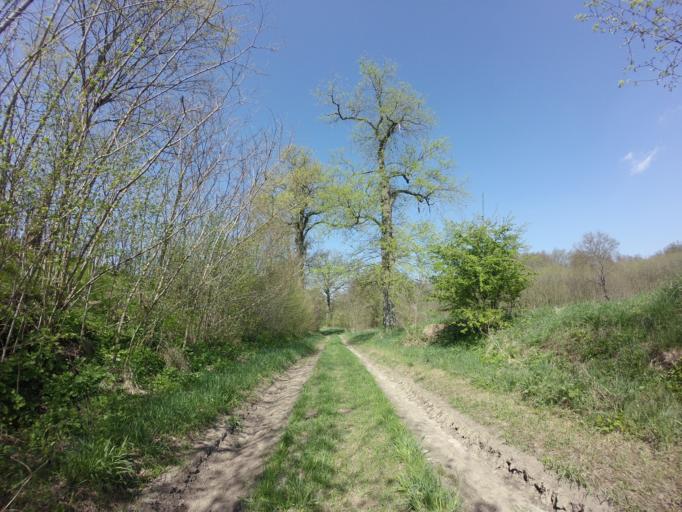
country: PL
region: West Pomeranian Voivodeship
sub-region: Powiat stargardzki
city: Suchan
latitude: 53.2225
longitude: 15.3435
